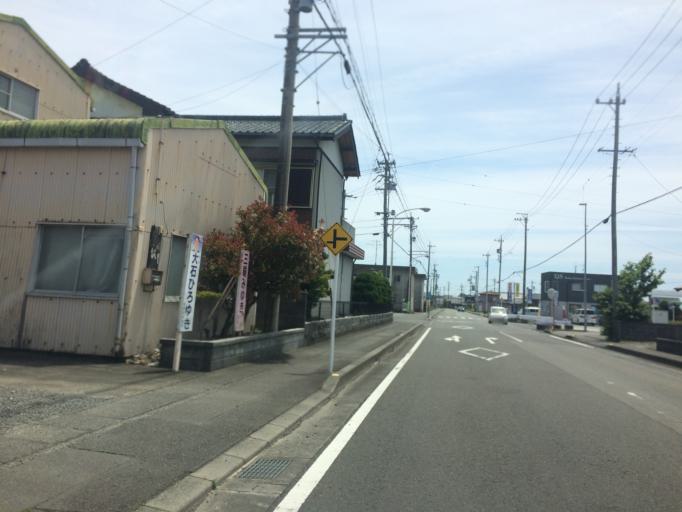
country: JP
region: Shizuoka
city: Sagara
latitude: 34.7595
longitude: 138.2597
